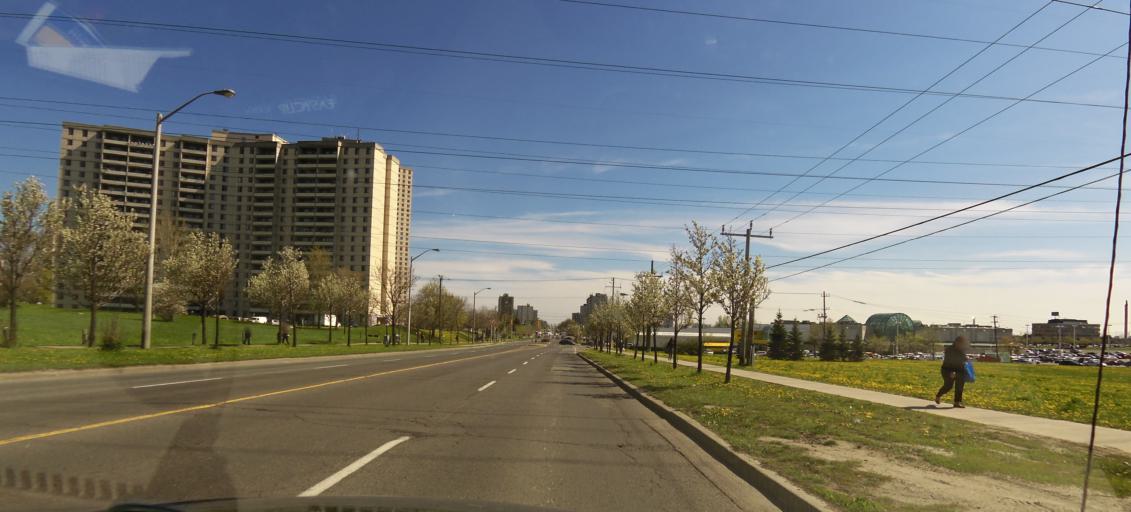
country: CA
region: Ontario
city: Concord
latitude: 43.7610
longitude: -79.5185
